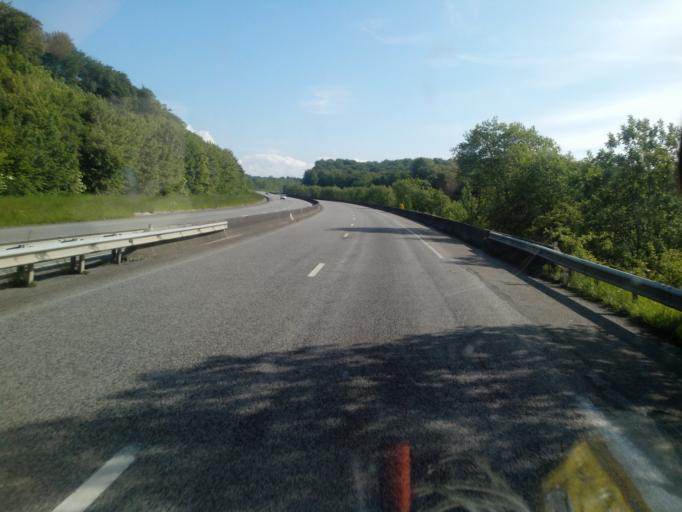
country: FR
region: Haute-Normandie
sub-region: Departement de la Seine-Maritime
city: Blangy-sur-Bresle
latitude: 49.9039
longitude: 1.6088
